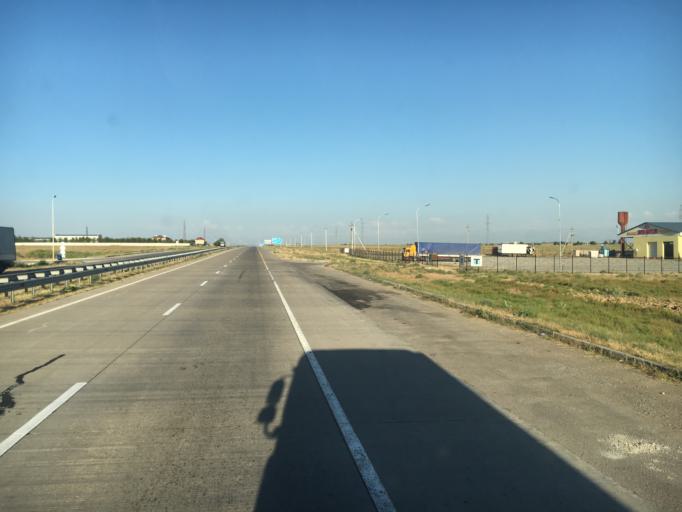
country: KZ
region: Ongtustik Qazaqstan
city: Shymkent
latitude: 42.4543
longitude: 69.6165
